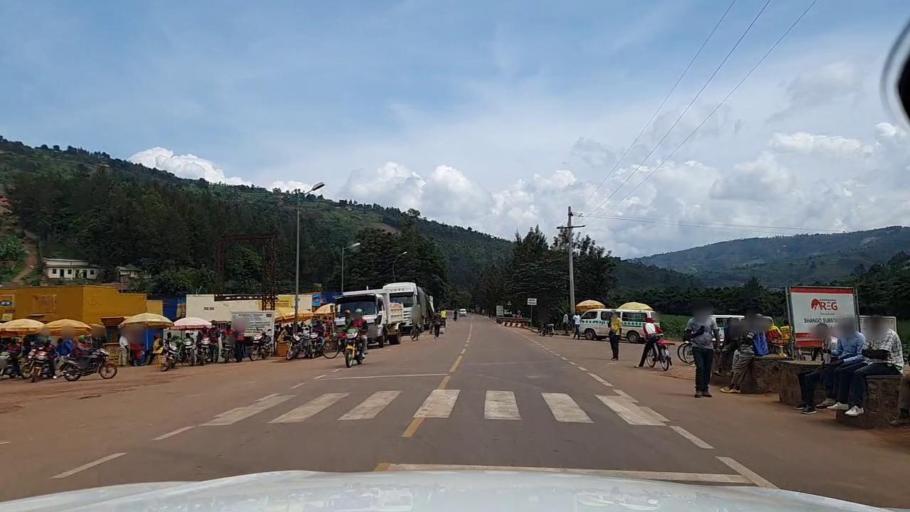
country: RW
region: Kigali
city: Kigali
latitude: -1.8667
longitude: 30.0870
